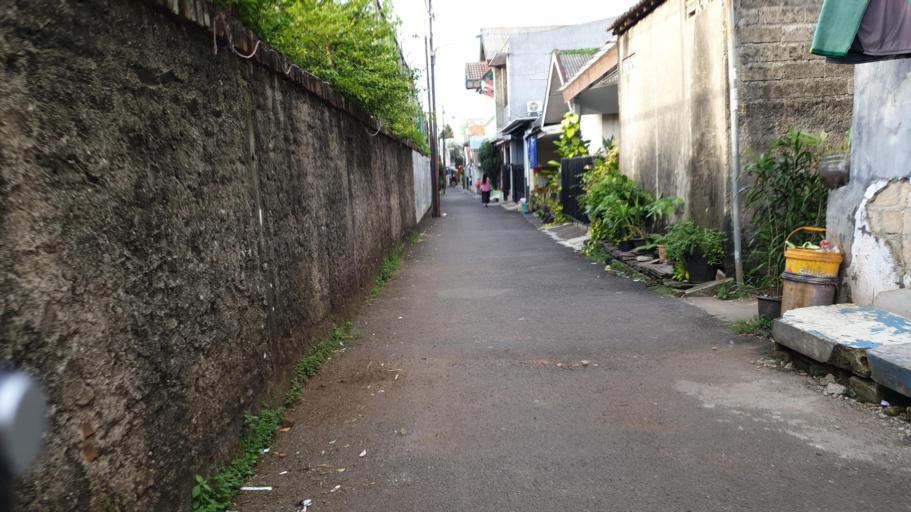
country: ID
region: Banten
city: South Tangerang
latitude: -6.2874
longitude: 106.7890
